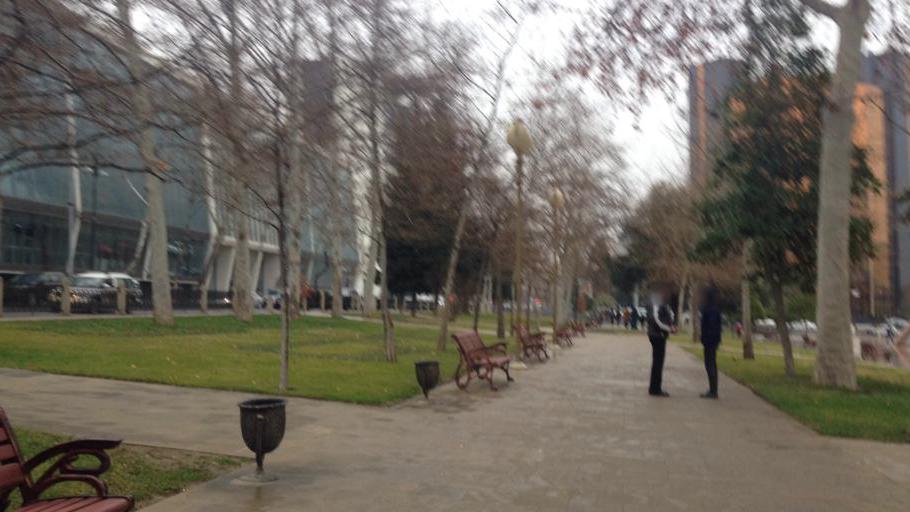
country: AZ
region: Baki
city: Baku
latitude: 40.3784
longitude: 49.8430
